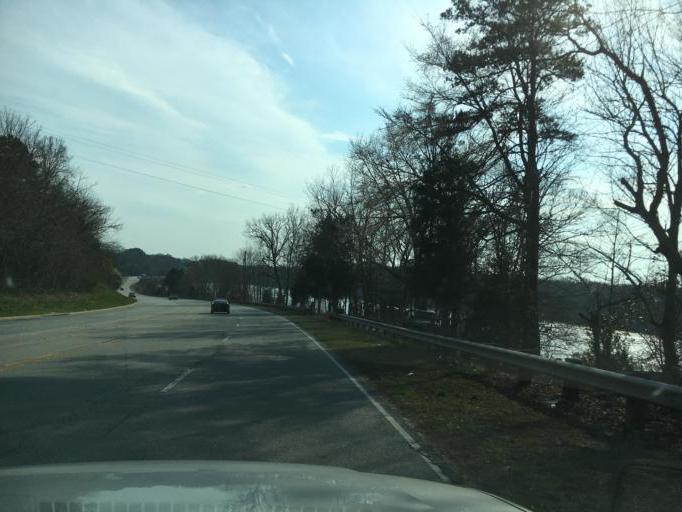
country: US
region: South Carolina
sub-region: Spartanburg County
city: Mayo
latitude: 35.0729
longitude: -81.8749
